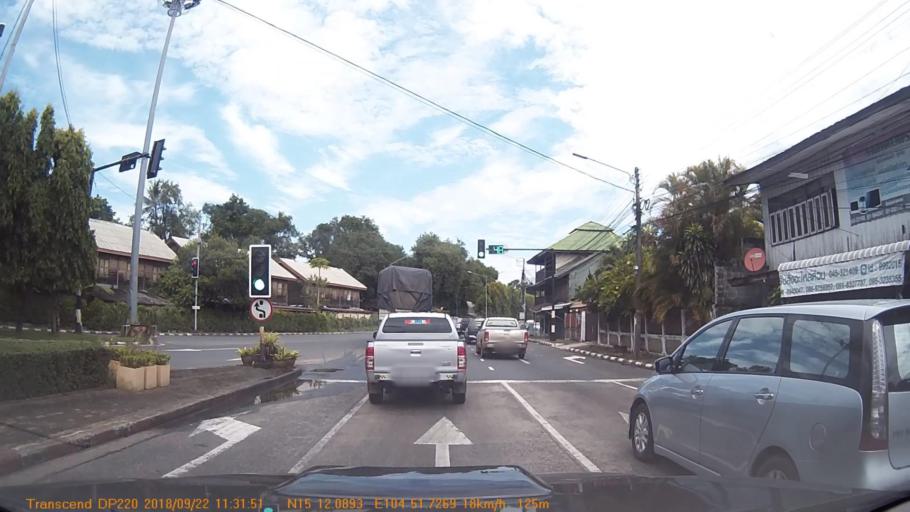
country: TH
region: Changwat Ubon Ratchathani
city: Warin Chamrap
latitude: 15.2016
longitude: 104.8621
